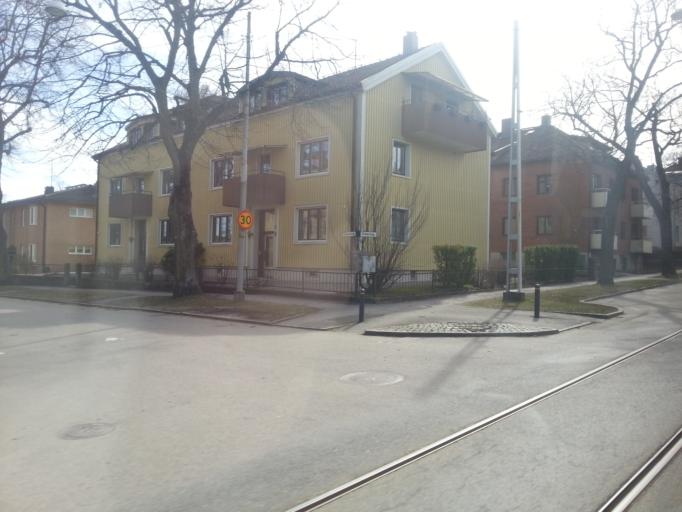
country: SE
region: OEstergoetland
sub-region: Norrkopings Kommun
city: Norrkoping
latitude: 58.5830
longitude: 16.1610
